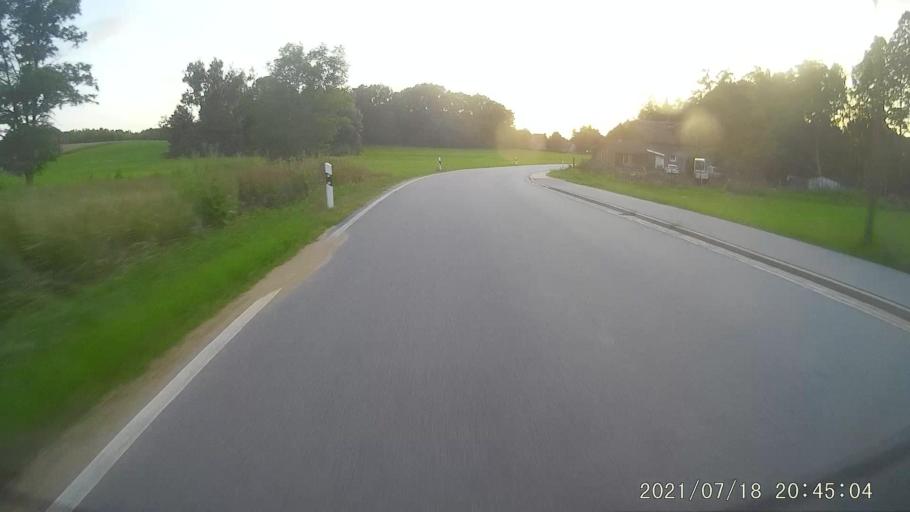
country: DE
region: Saxony
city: Reichenbach
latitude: 51.1957
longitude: 14.7807
